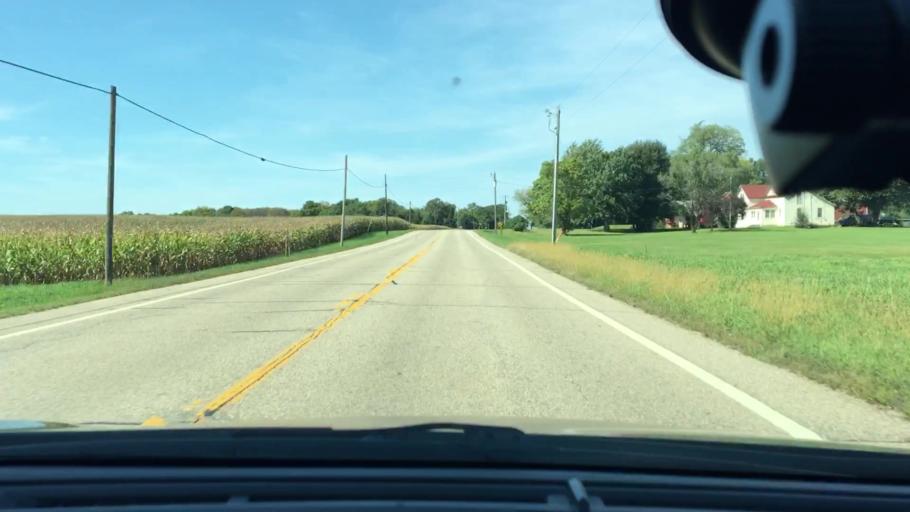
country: US
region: Minnesota
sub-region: Hennepin County
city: Corcoran
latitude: 45.1131
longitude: -93.5795
